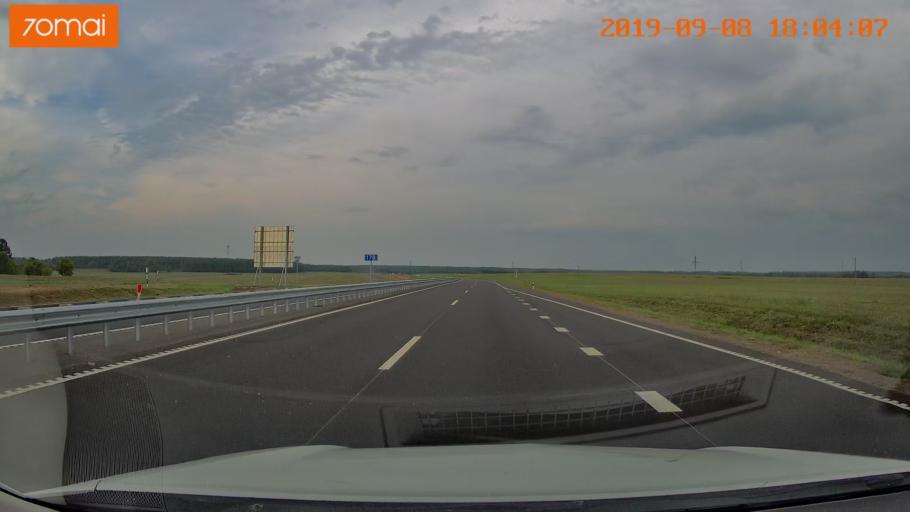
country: BY
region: Grodnenskaya
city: Lida
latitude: 53.8119
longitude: 25.1137
